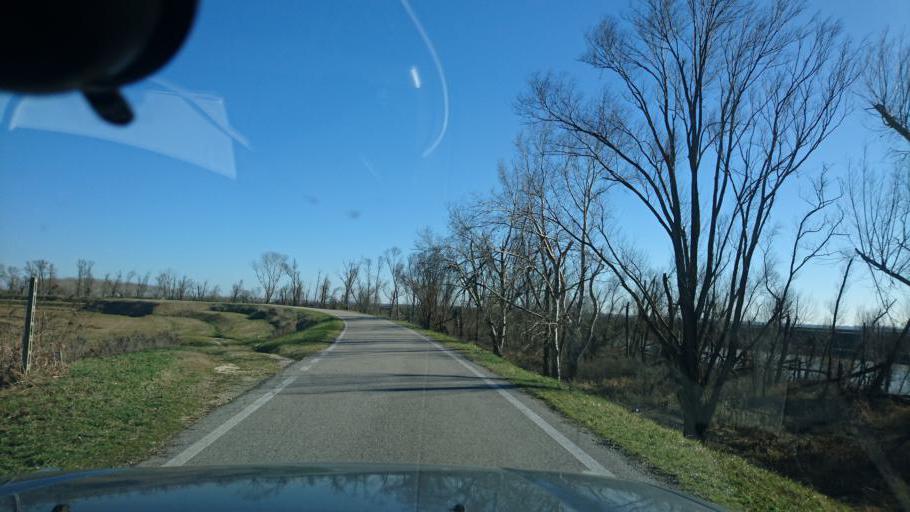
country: IT
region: Veneto
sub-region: Provincia di Rovigo
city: Ariano
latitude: 44.9289
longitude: 12.1413
